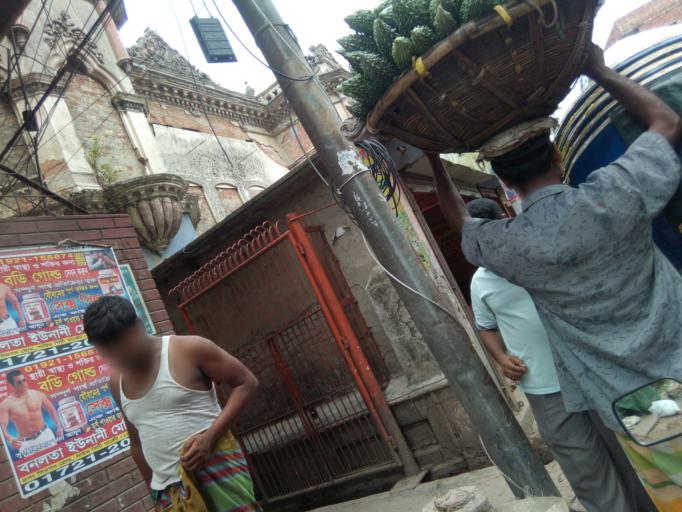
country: BD
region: Dhaka
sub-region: Dhaka
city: Dhaka
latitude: 23.7023
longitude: 90.4156
